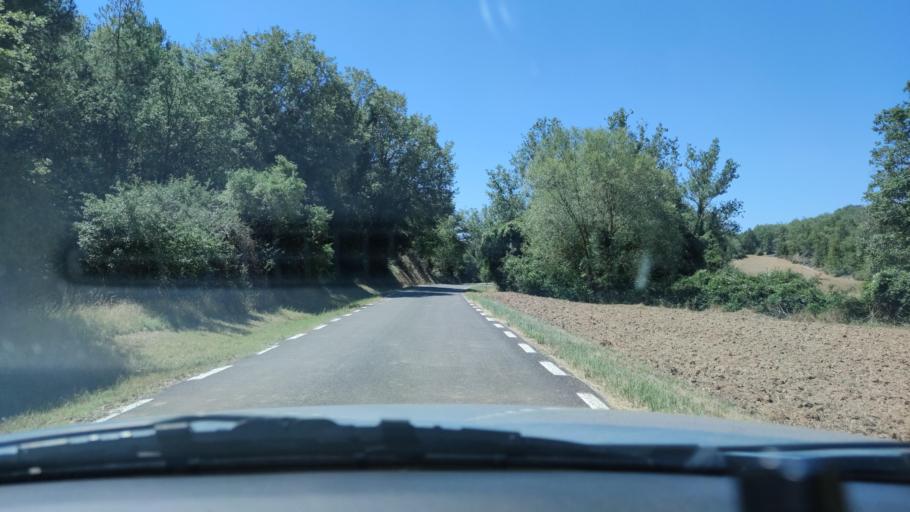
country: ES
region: Catalonia
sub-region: Provincia de Lleida
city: Tora de Riubregos
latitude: 41.9107
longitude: 1.4497
